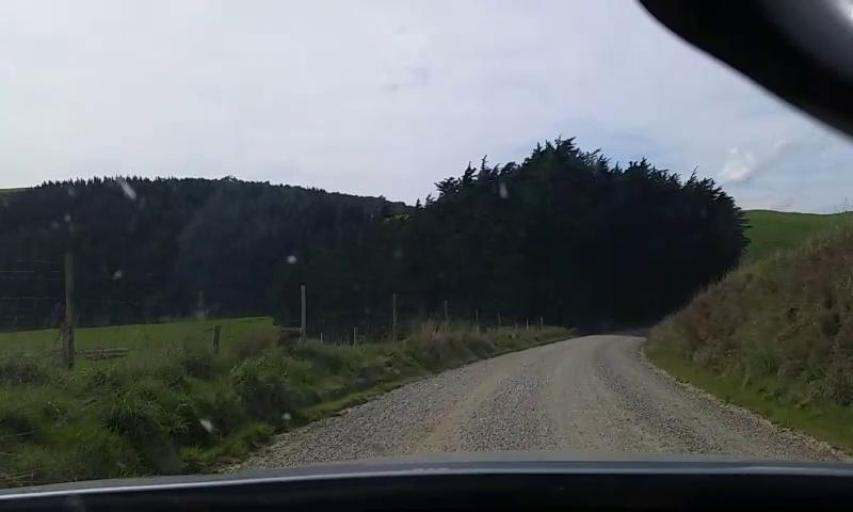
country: NZ
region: Otago
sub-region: Clutha District
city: Papatowai
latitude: -46.6263
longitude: 168.9942
